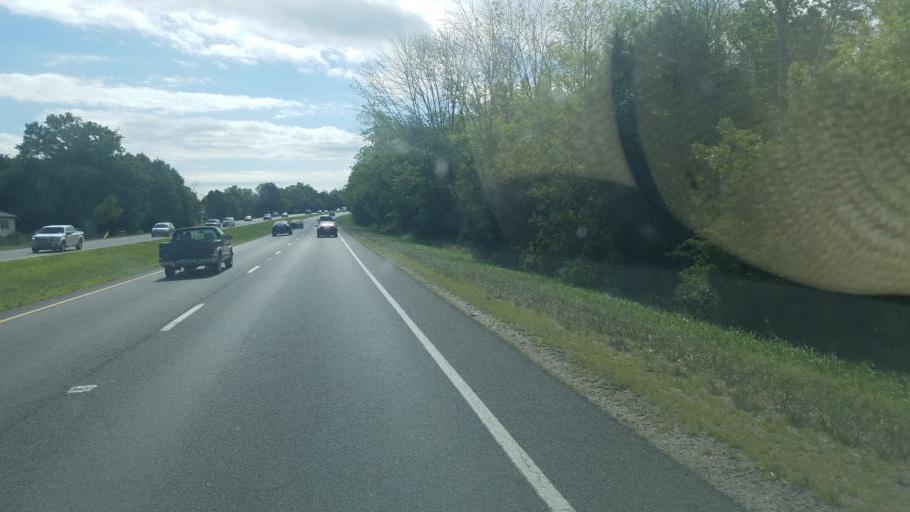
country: US
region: Virginia
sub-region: Fauquier County
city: Bealeton
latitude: 38.5613
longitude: -77.7442
